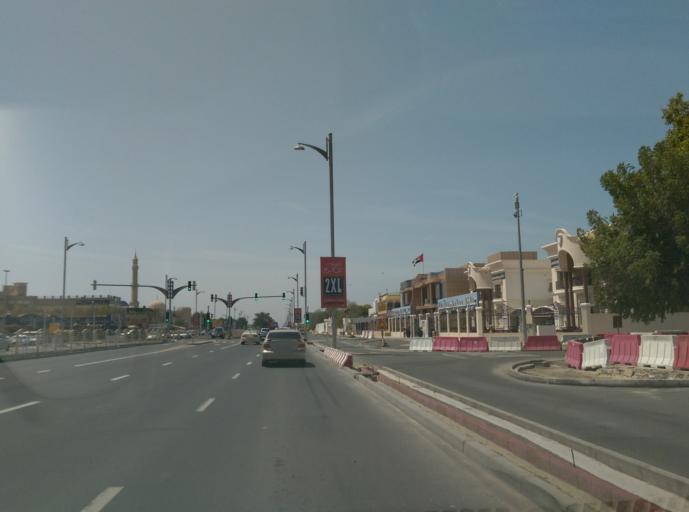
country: AE
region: Dubai
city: Dubai
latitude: 25.1877
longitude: 55.2296
